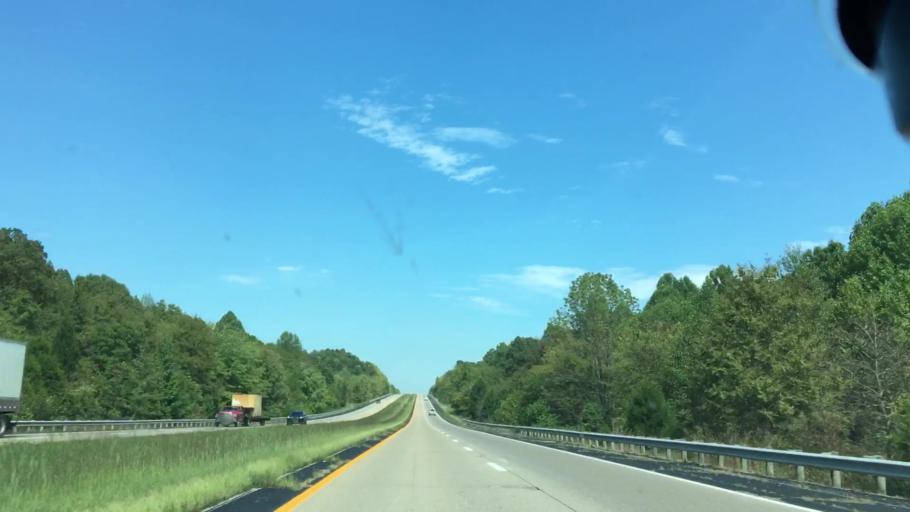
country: US
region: Kentucky
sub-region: Hopkins County
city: Nortonville
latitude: 37.1006
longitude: -87.4608
